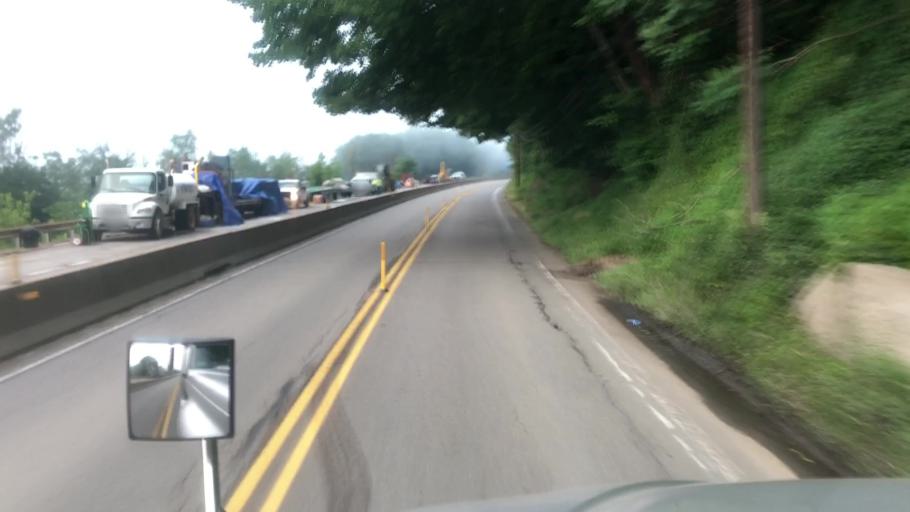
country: US
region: Pennsylvania
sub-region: Venango County
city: Woodland Heights
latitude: 41.4102
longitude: -79.7352
